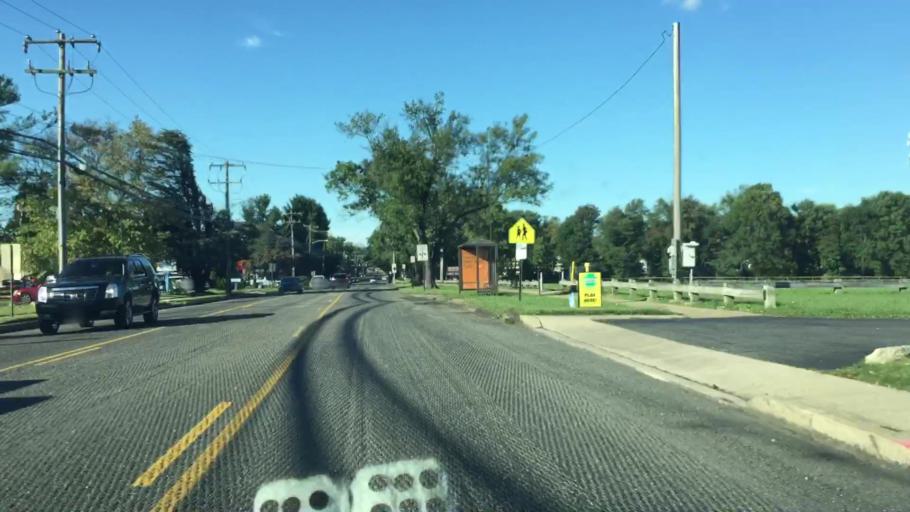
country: US
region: Pennsylvania
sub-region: Delaware County
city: Boothwyn
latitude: 39.8366
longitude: -75.4422
